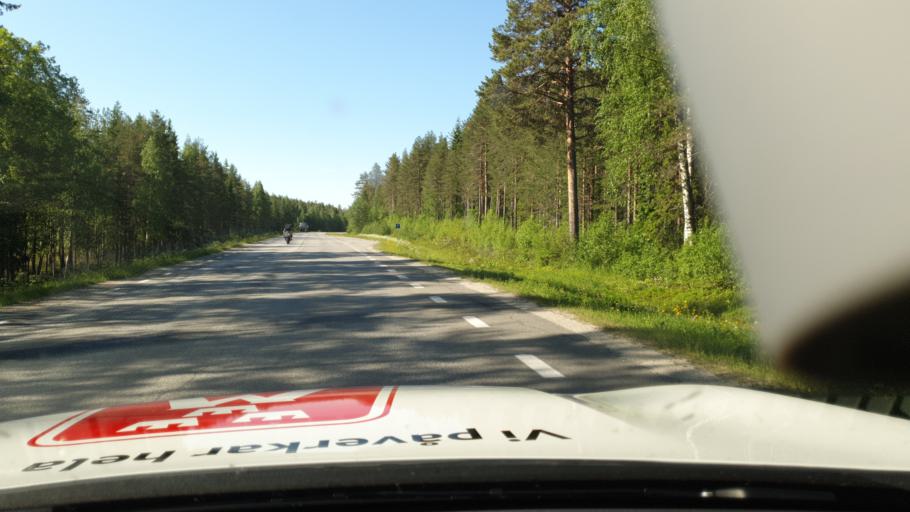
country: SE
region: Vaesterbotten
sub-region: Lycksele Kommun
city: Lycksele
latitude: 64.5829
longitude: 18.6589
